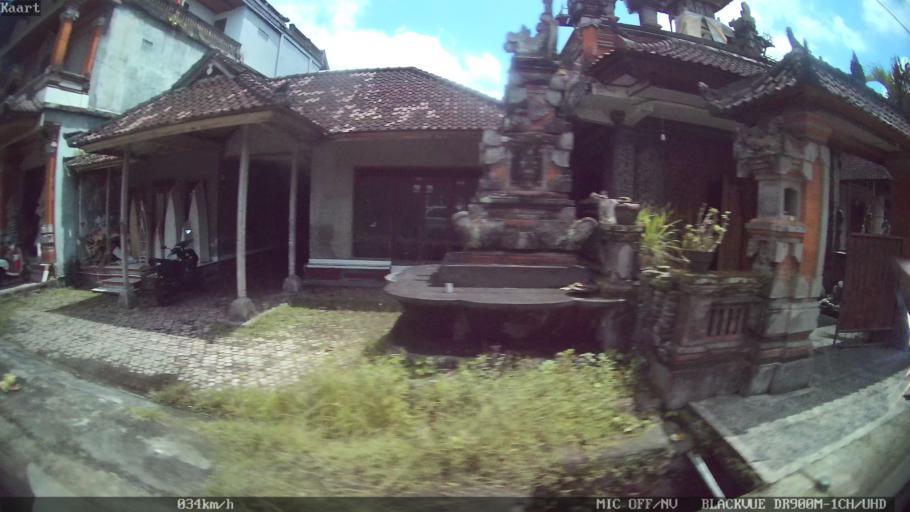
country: ID
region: Bali
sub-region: Kabupaten Gianyar
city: Ubud
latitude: -8.5322
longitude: 115.2821
